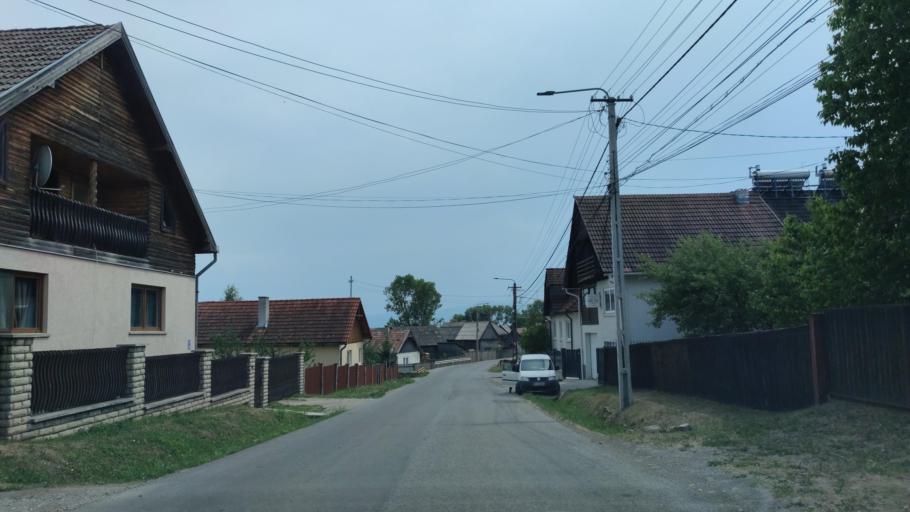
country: RO
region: Harghita
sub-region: Comuna Remetea
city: Remetea
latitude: 46.8060
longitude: 25.4602
